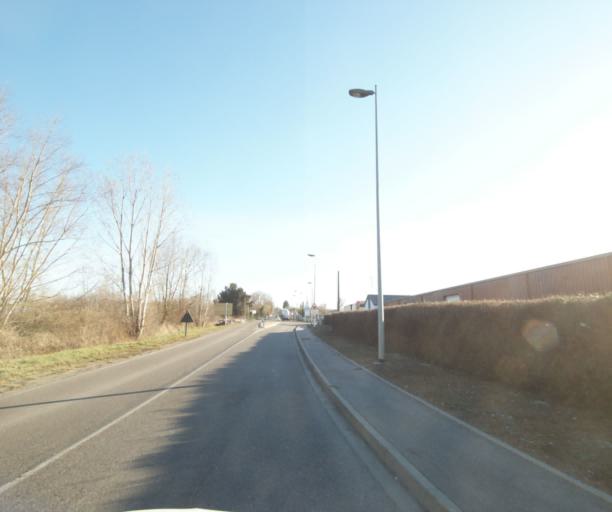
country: FR
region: Lorraine
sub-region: Departement de Meurthe-et-Moselle
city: Art-sur-Meurthe
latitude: 48.6430
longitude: 6.2534
